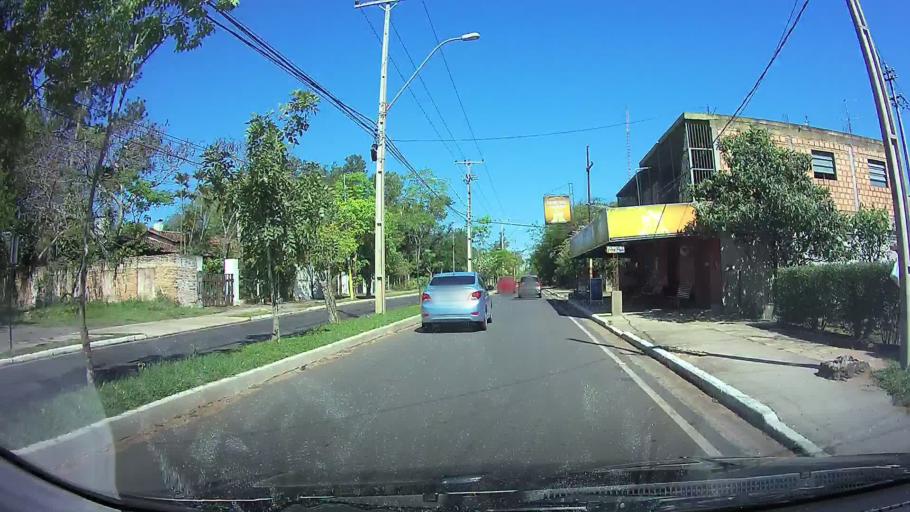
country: PY
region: Cordillera
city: San Bernardino
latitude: -25.2979
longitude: -57.3040
